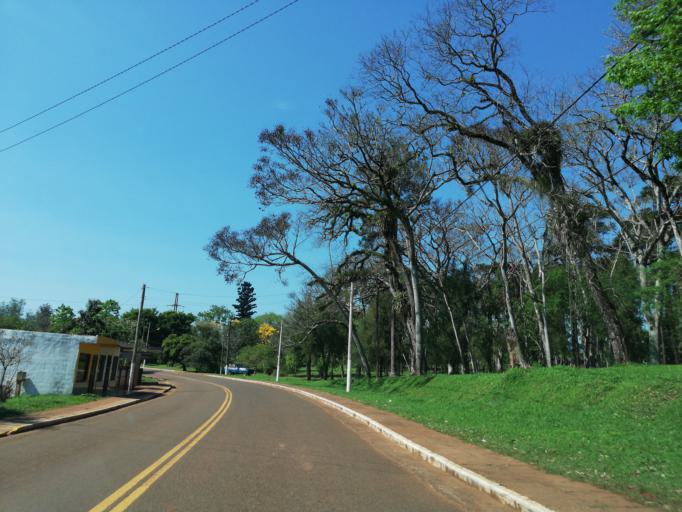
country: AR
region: Misiones
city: Puerto Eldorado
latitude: -26.4104
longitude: -54.6891
